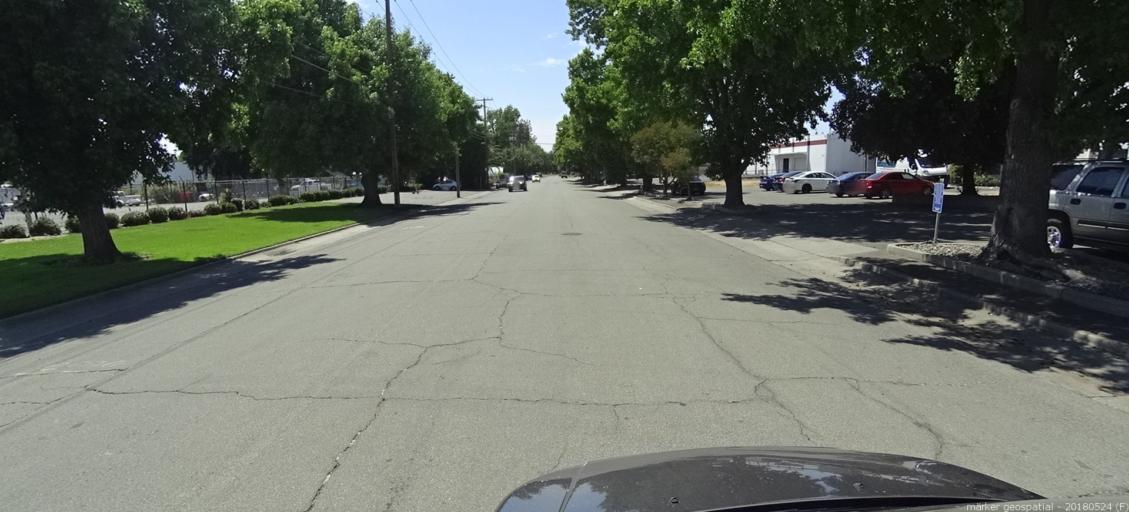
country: US
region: California
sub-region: Sacramento County
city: Sacramento
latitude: 38.5972
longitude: -121.4605
